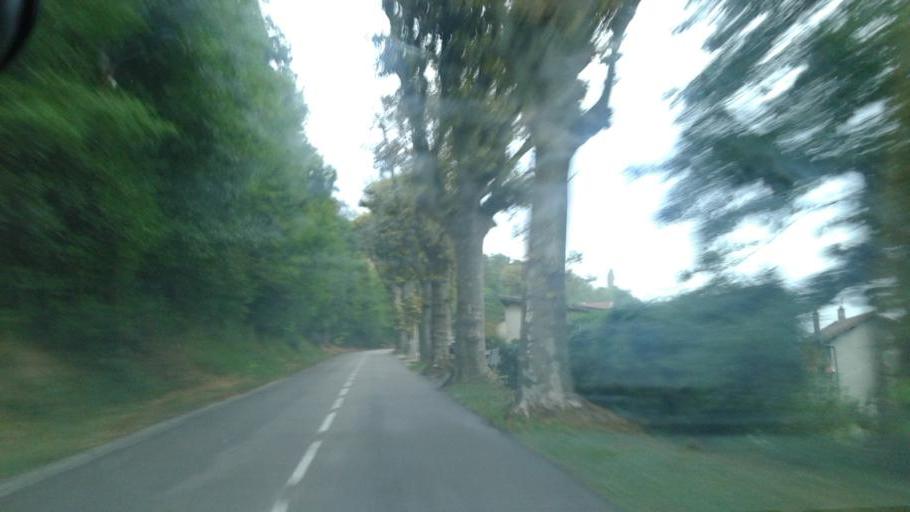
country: FR
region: Rhone-Alpes
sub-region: Departement de l'Ain
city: Miribel
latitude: 45.8257
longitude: 4.9439
